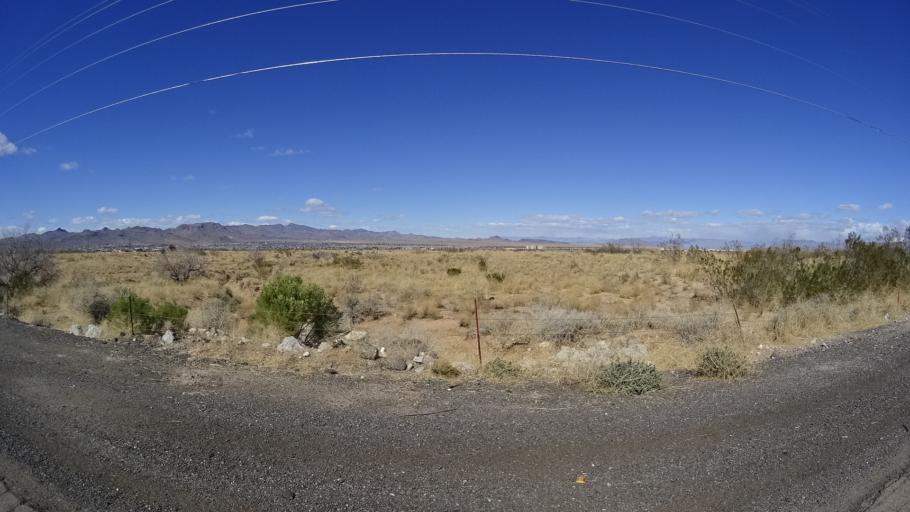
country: US
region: Arizona
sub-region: Mohave County
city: Kingman
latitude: 35.2008
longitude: -113.9853
